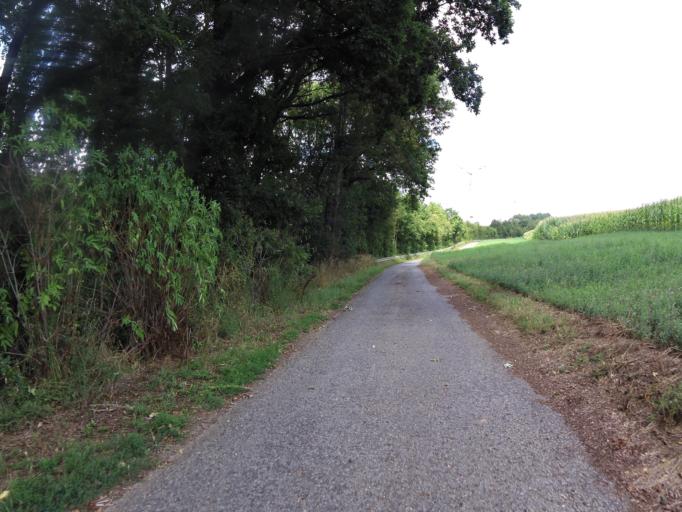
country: DE
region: Bavaria
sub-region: Regierungsbezirk Unterfranken
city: Sommerhausen
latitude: 49.7087
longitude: 10.0311
